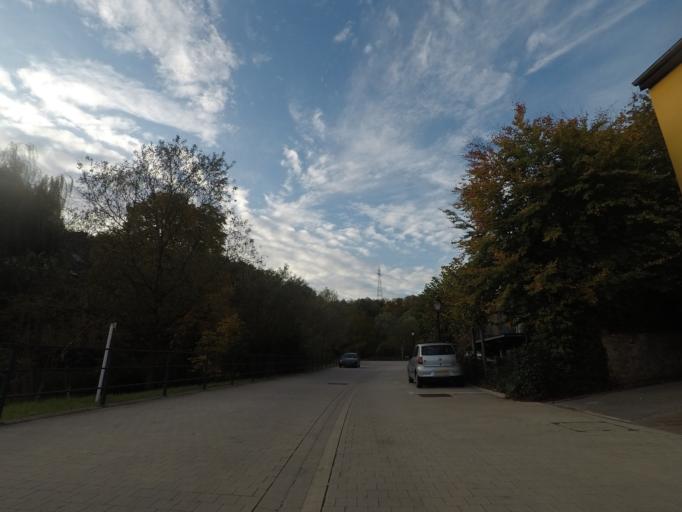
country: LU
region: Luxembourg
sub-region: Canton de Luxembourg
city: Hesperange
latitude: 49.5739
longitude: 6.1556
